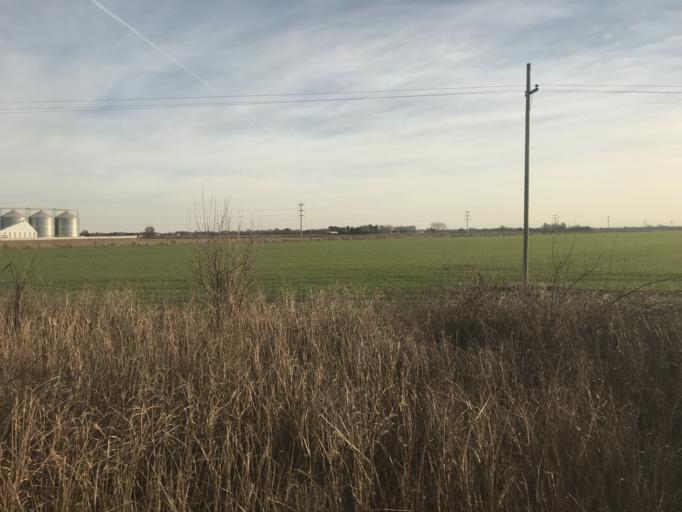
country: AR
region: Cordoba
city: Malvinas Argentinas
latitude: -31.4734
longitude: -64.0944
